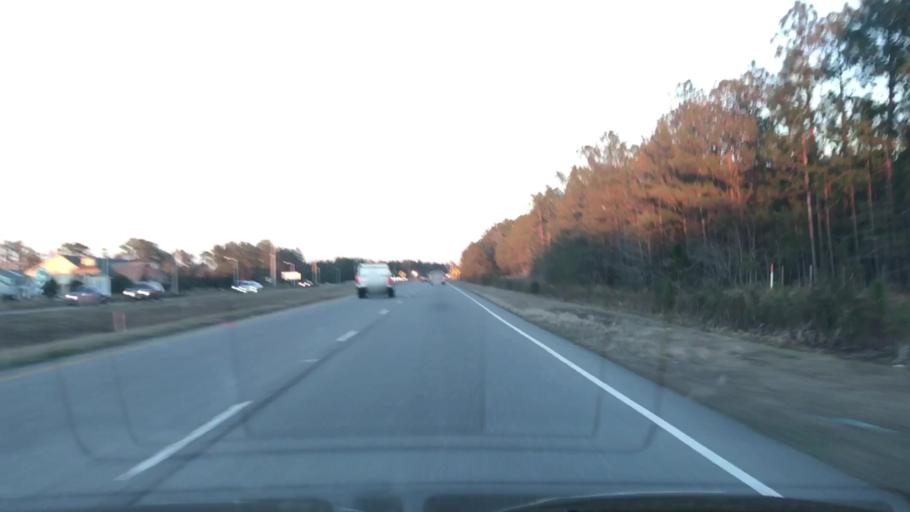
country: US
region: North Carolina
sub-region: Brunswick County
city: Shallotte
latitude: 33.9837
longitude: -78.3952
